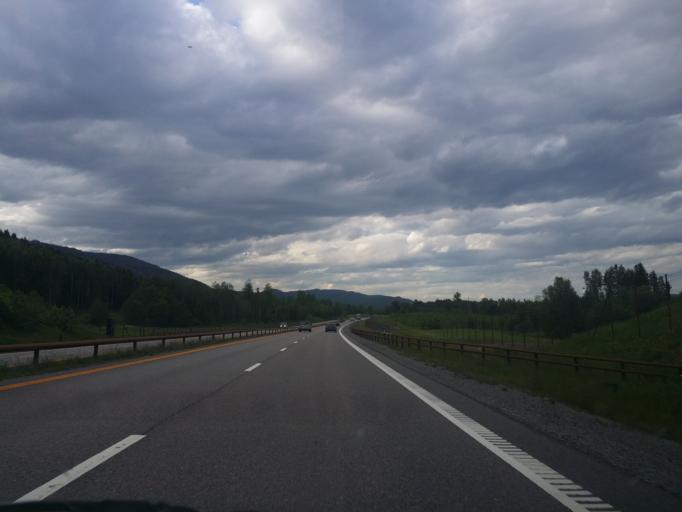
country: NO
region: Akershus
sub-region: Eidsvoll
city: Eidsvoll
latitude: 60.3569
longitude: 11.2061
